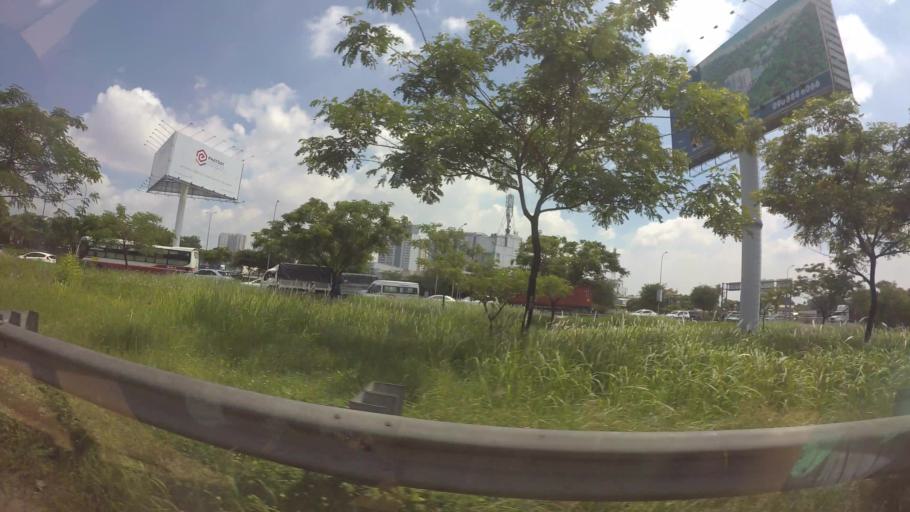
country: VN
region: Ho Chi Minh City
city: Quan Hai
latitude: 10.7936
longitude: 106.7563
